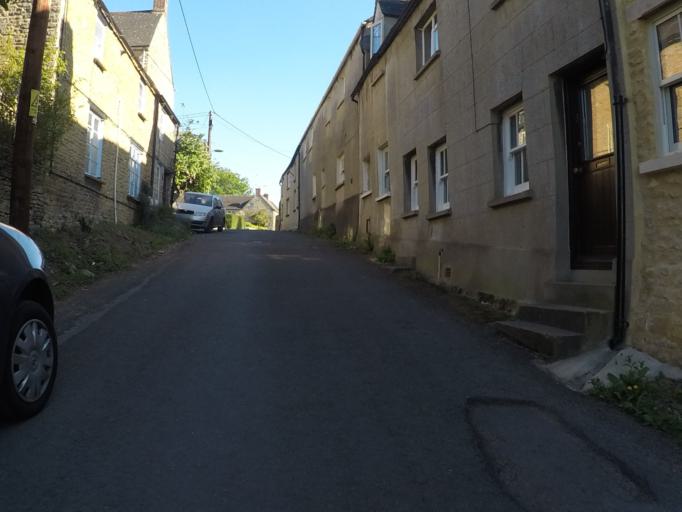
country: GB
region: England
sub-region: Oxfordshire
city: Charlbury
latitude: 51.8705
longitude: -1.4802
